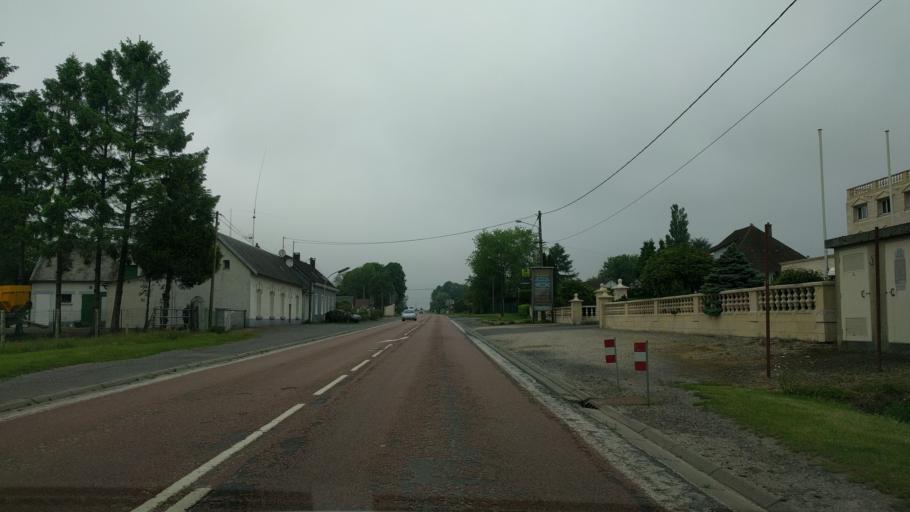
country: FR
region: Picardie
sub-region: Departement de la Somme
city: Moislains
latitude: 50.0026
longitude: 2.9099
